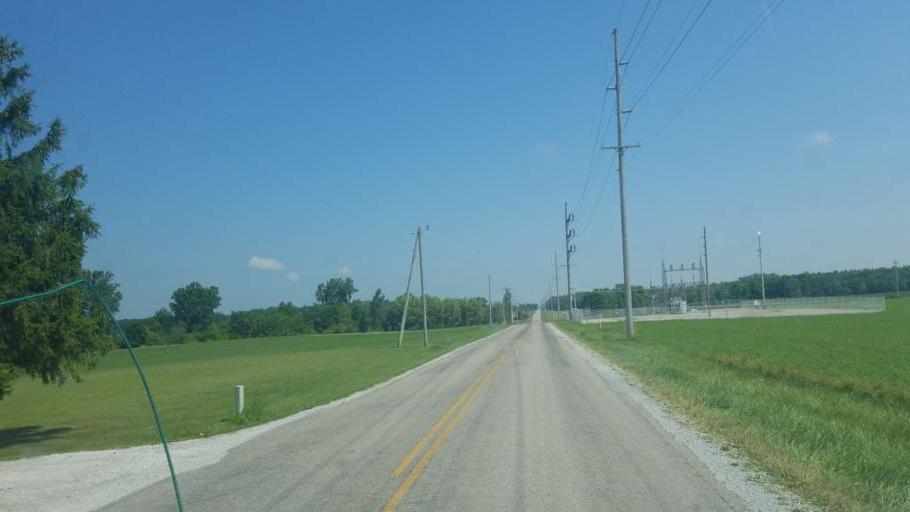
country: US
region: Ohio
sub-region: Hardin County
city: Kenton
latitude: 40.6997
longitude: -83.6537
